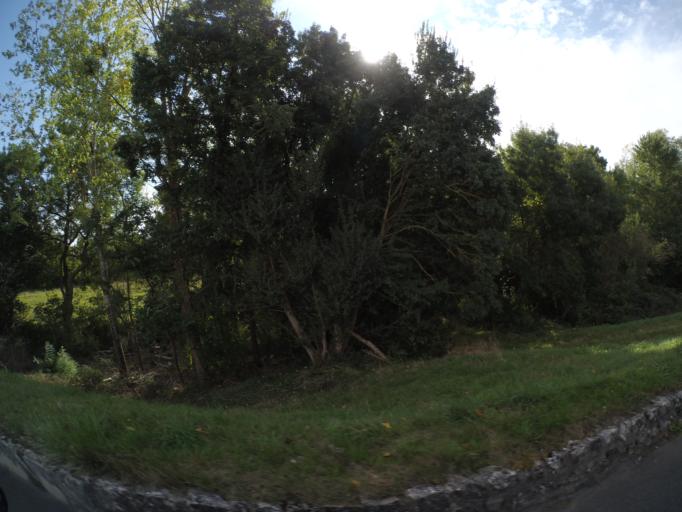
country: FR
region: Pays de la Loire
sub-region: Departement de Maine-et-Loire
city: Varennes-sur-Loire
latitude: 47.2264
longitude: 0.0706
